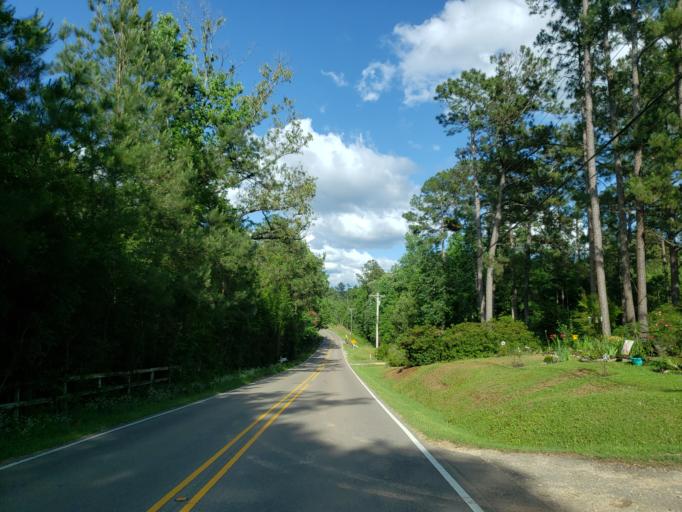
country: US
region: Mississippi
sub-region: Lamar County
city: West Hattiesburg
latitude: 31.2726
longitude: -89.3995
